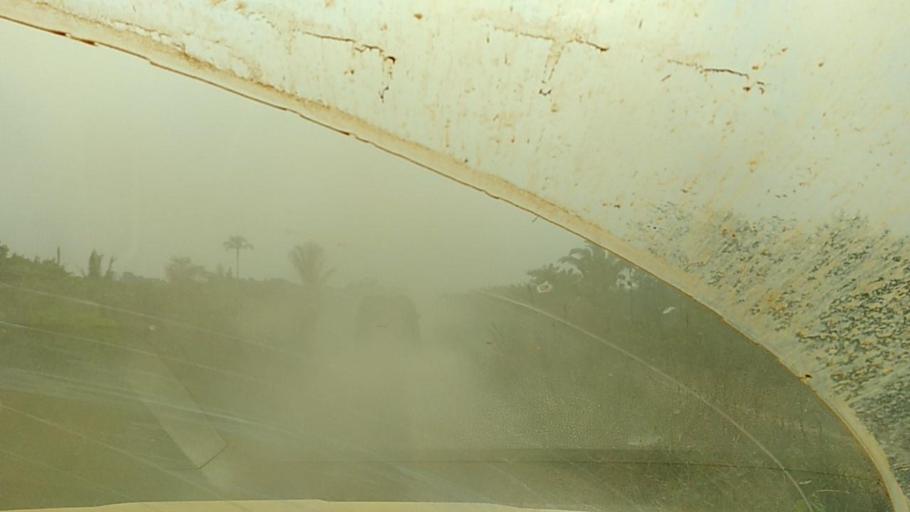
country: BR
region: Rondonia
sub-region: Porto Velho
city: Porto Velho
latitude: -8.7735
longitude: -63.1762
